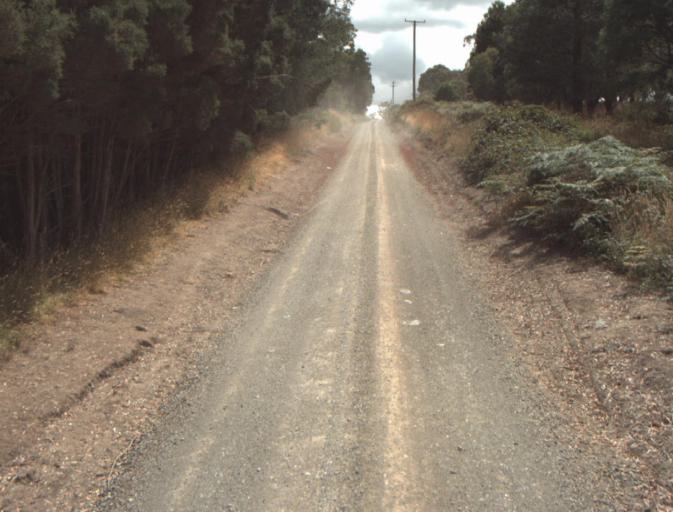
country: AU
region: Tasmania
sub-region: Launceston
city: Mayfield
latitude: -41.1957
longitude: 147.1700
